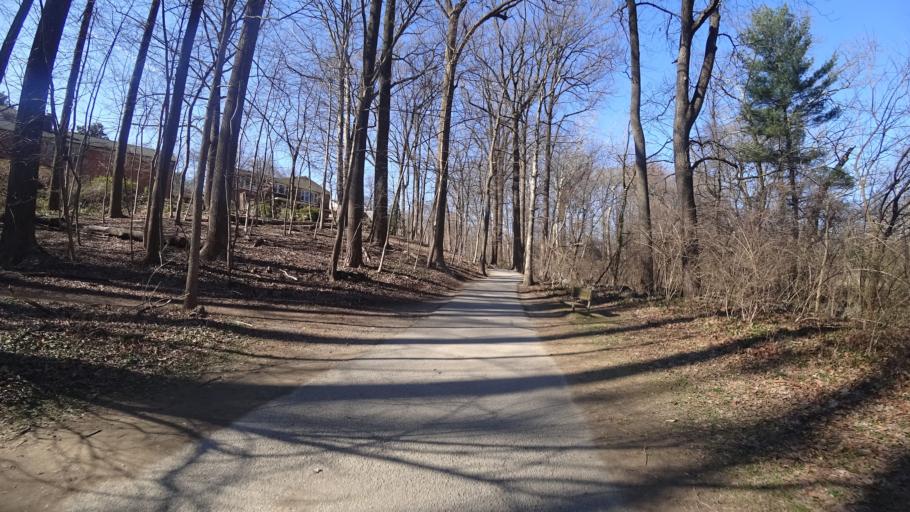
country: US
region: Maryland
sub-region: Montgomery County
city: Four Corners
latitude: 39.0108
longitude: -77.0274
